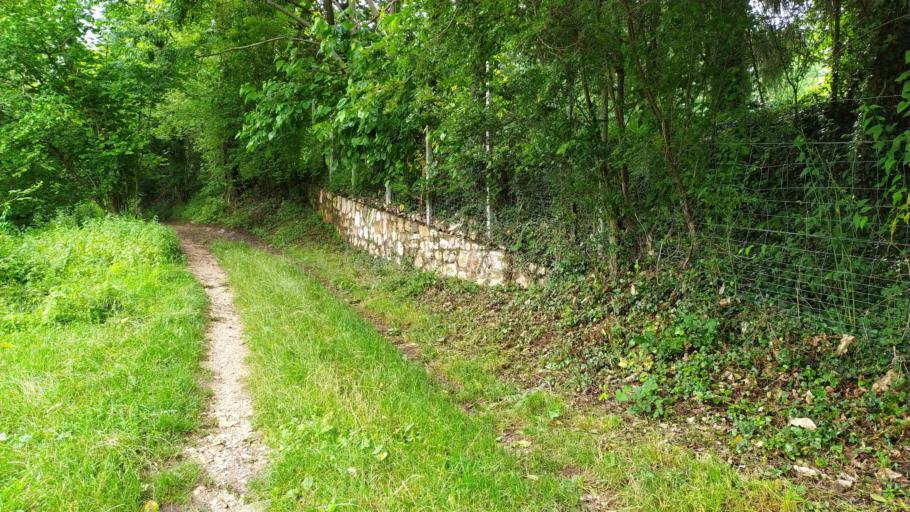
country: IT
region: Veneto
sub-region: Provincia di Vicenza
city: Torrebelvicino
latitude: 45.6938
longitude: 11.3181
